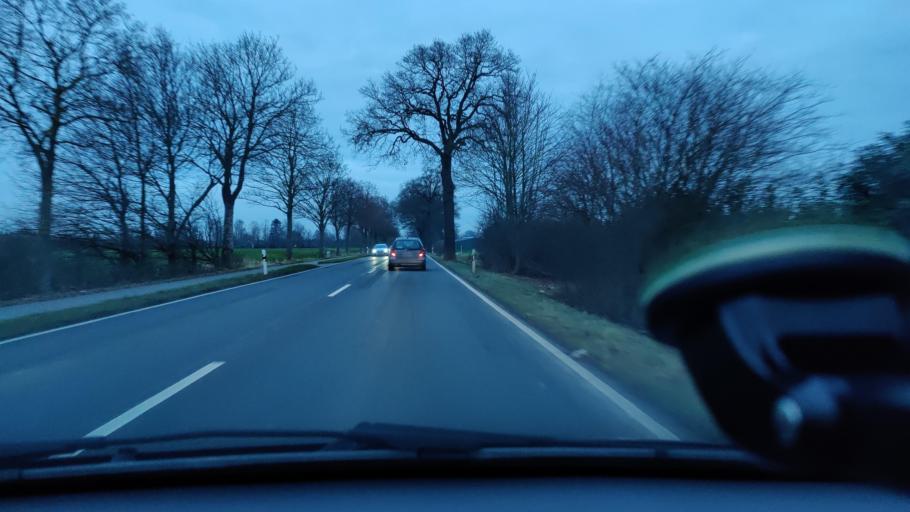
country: DE
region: North Rhine-Westphalia
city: Straelen
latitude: 51.4809
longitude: 6.2930
